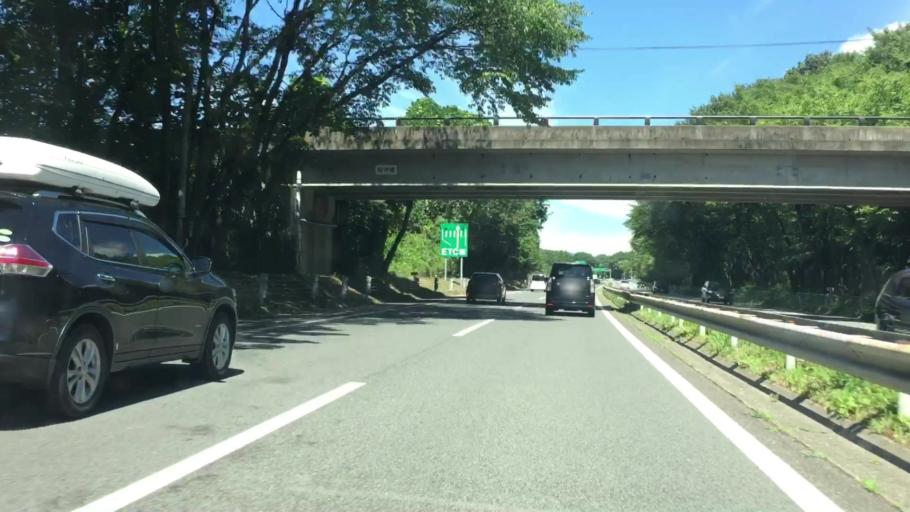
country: JP
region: Tochigi
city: Imaichi
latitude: 36.6804
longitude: 139.7612
